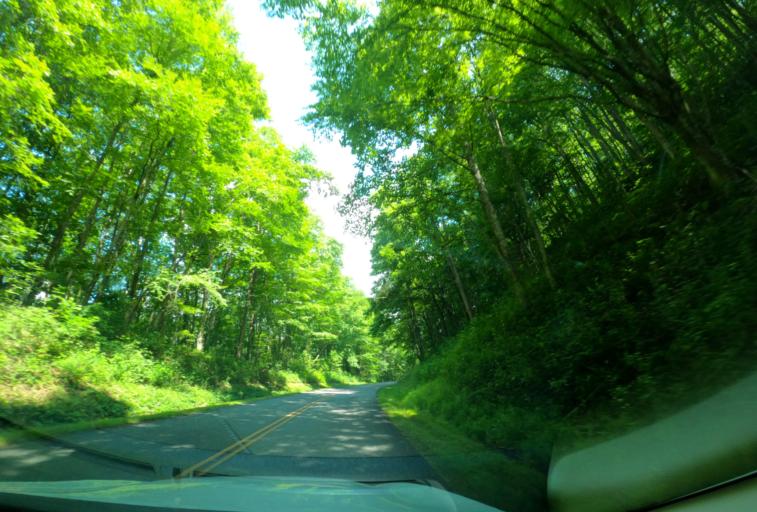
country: US
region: North Carolina
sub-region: Haywood County
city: Hazelwood
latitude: 35.4357
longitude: -83.0798
